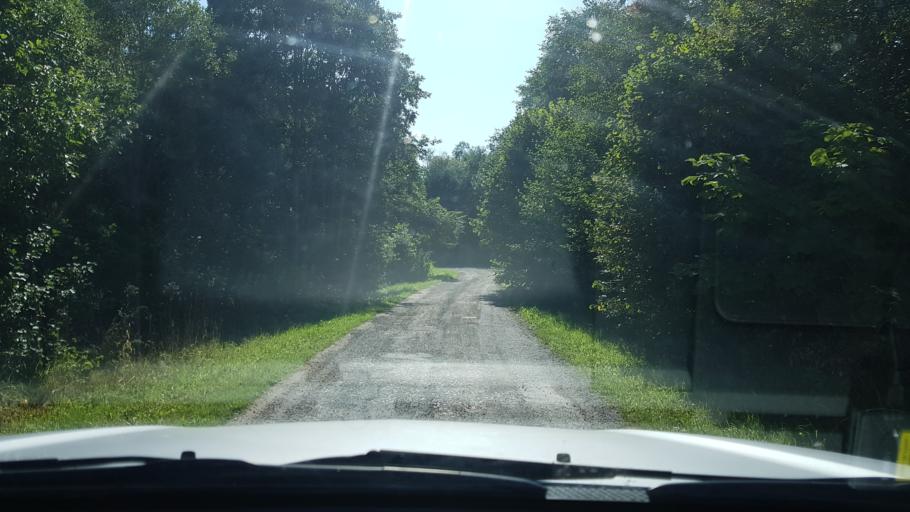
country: EE
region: Ida-Virumaa
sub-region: Sillamaee linn
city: Sillamae
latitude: 59.3901
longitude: 27.8766
